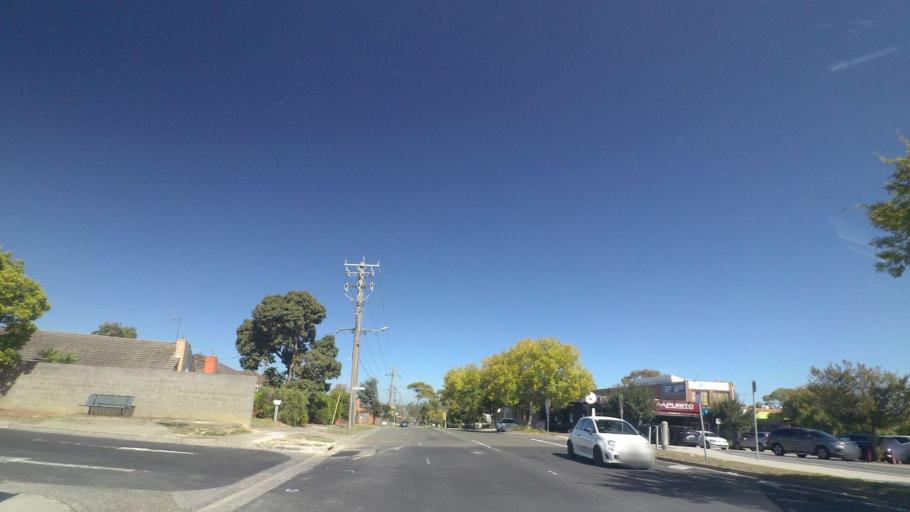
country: AU
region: Victoria
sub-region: Manningham
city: Donvale
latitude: -37.7915
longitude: 145.1708
